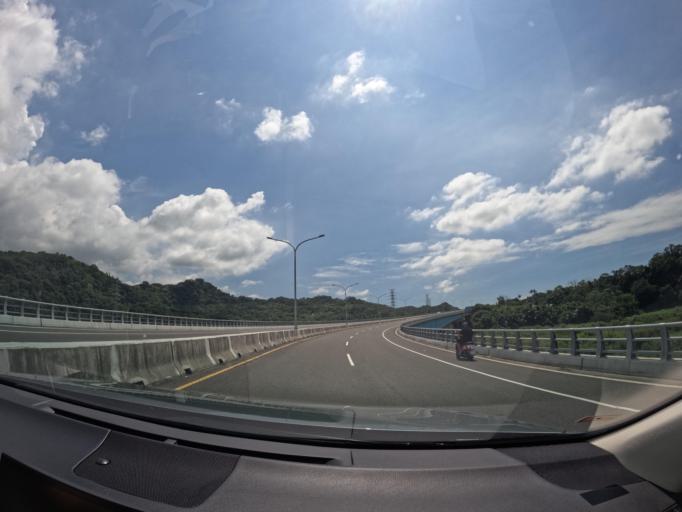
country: TW
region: Taiwan
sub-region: Hsinchu
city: Hsinchu
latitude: 24.6727
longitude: 120.9478
